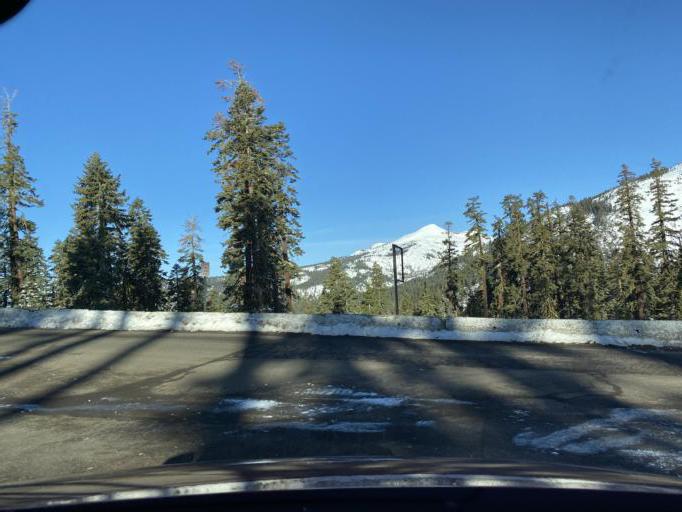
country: US
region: California
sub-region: El Dorado County
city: South Lake Tahoe
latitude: 38.8020
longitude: -120.0843
